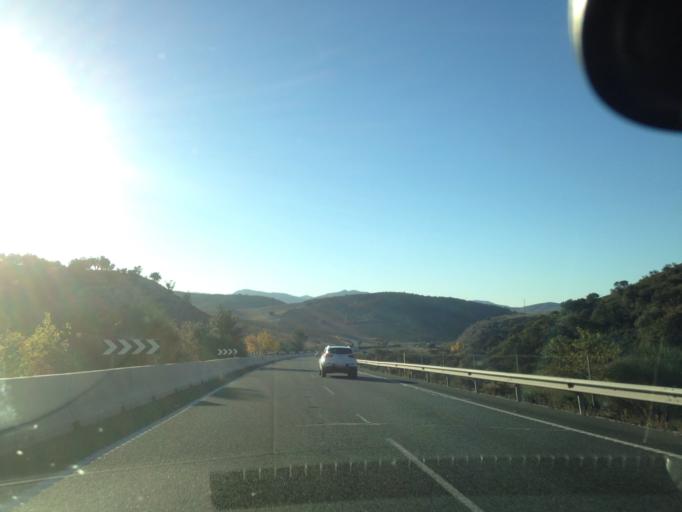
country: ES
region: Andalusia
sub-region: Provincia de Malaga
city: Casabermeja
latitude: 36.9464
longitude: -4.4415
